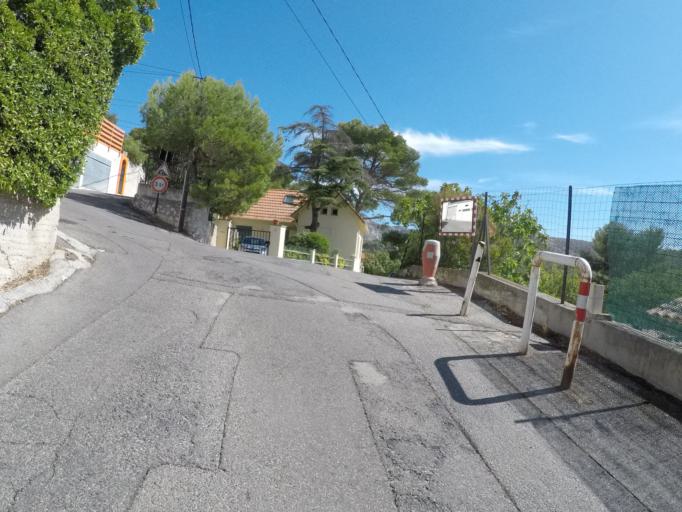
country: FR
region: Provence-Alpes-Cote d'Azur
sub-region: Departement des Bouches-du-Rhone
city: Marseille 09
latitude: 43.2468
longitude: 5.4303
